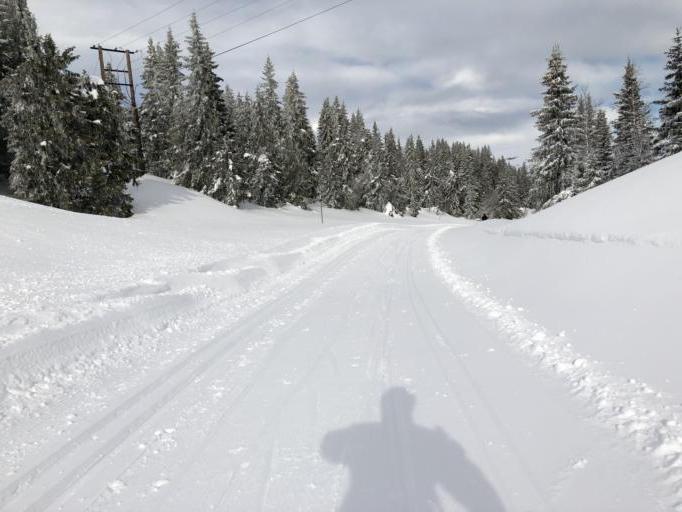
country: NO
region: Oppland
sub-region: Gausdal
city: Segalstad bru
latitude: 61.3125
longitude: 10.0719
